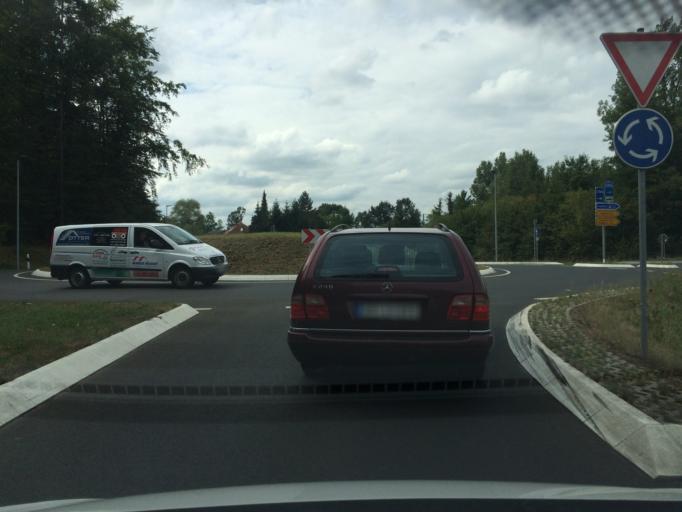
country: DE
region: Bavaria
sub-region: Regierungsbezirk Unterfranken
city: Sailauf
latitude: 49.9981
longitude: 9.2379
